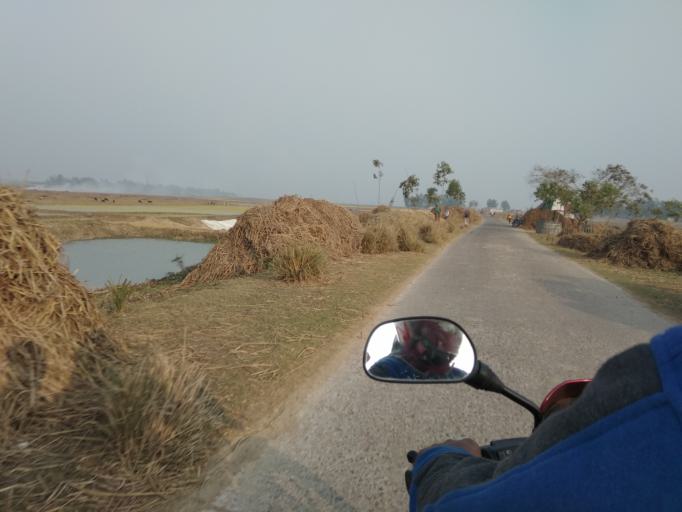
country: BD
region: Rajshahi
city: Ishurdi
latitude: 24.4947
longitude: 89.1941
